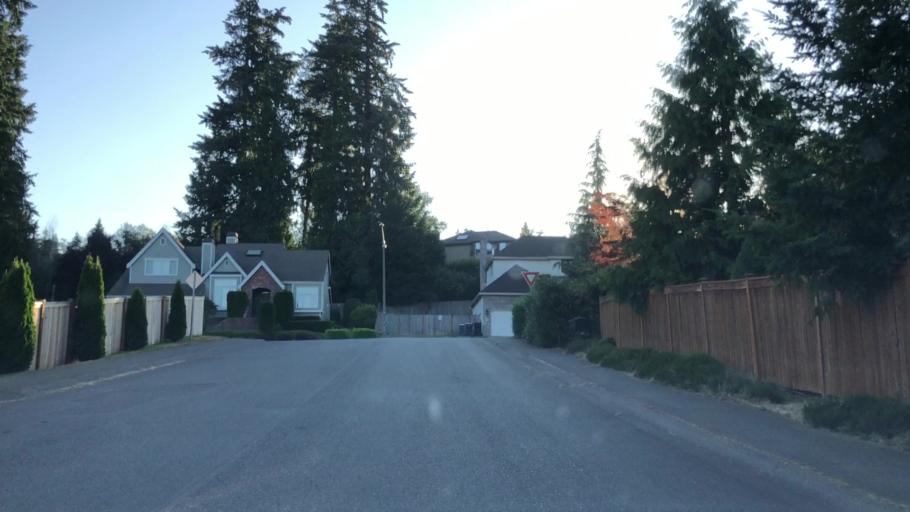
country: US
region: Washington
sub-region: King County
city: Redmond
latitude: 47.6901
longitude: -122.0950
